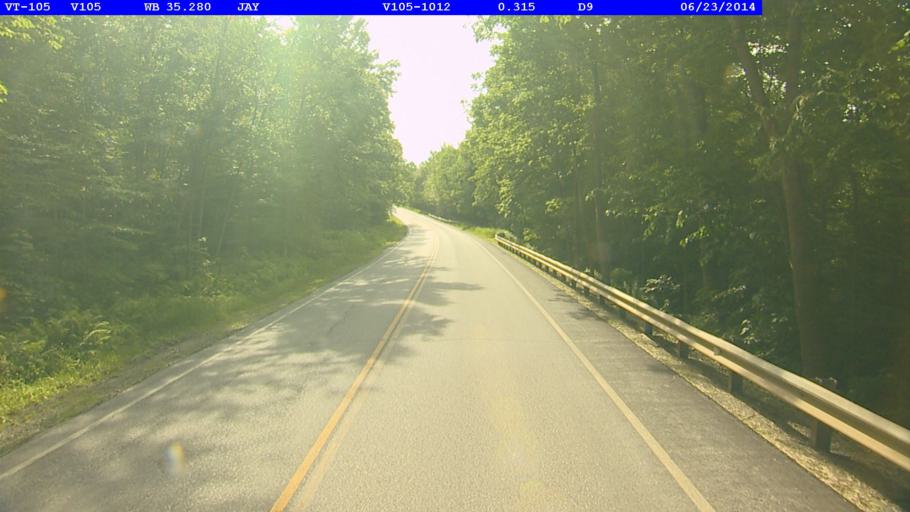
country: US
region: Vermont
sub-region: Franklin County
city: Richford
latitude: 44.9860
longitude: -72.5428
